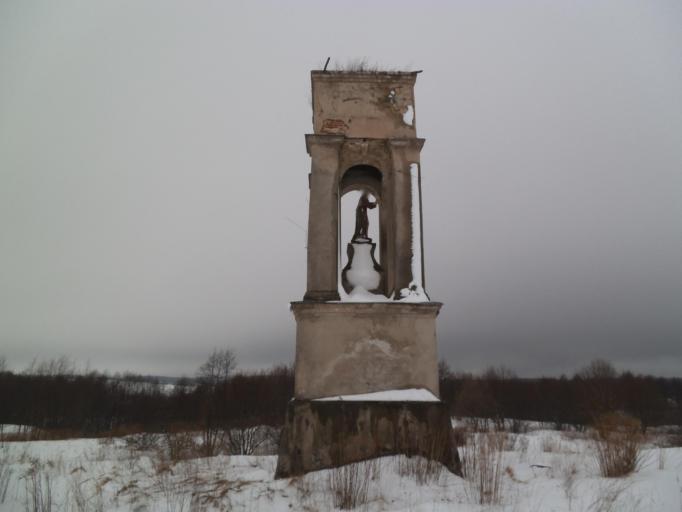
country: LT
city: Skaidiskes
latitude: 54.4603
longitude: 25.4778
